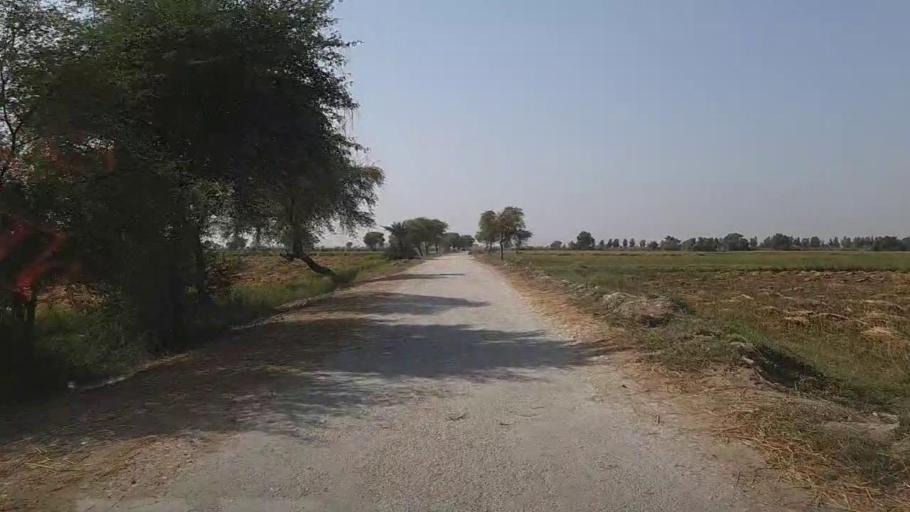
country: PK
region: Sindh
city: Kandhkot
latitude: 28.3938
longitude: 69.3176
